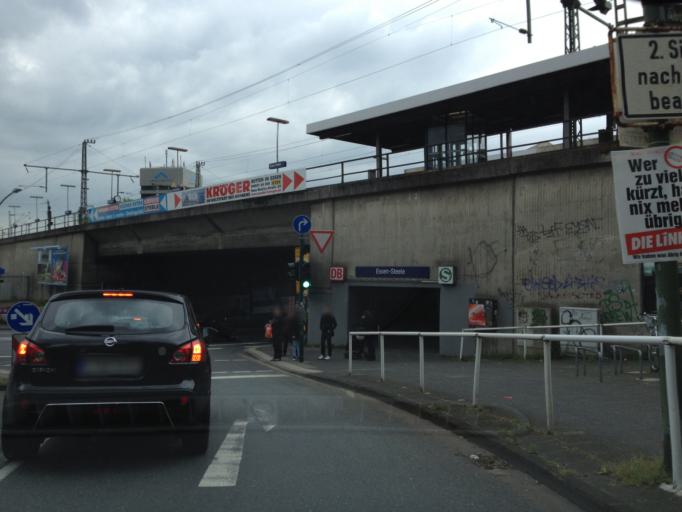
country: DE
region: North Rhine-Westphalia
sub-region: Regierungsbezirk Dusseldorf
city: Essen
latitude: 51.4511
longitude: 7.0762
